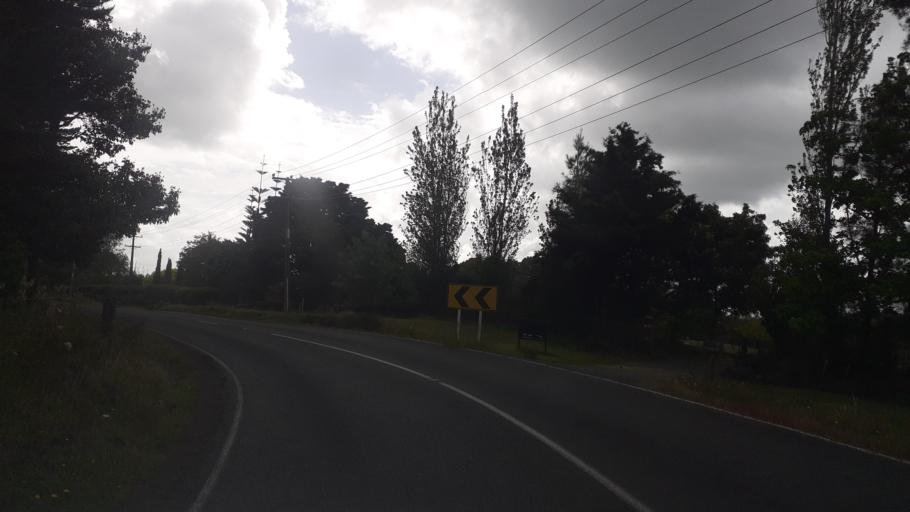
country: NZ
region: Northland
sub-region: Far North District
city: Kerikeri
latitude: -35.2250
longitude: 174.0220
